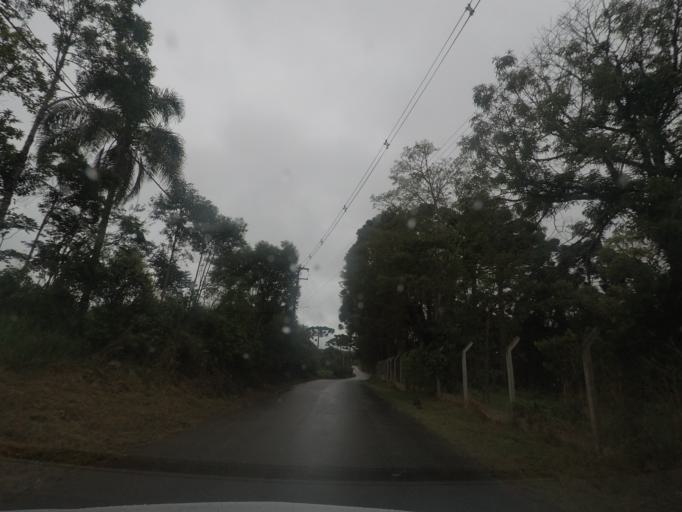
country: BR
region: Parana
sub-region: Campina Grande Do Sul
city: Campina Grande do Sul
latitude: -25.3029
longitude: -49.1319
